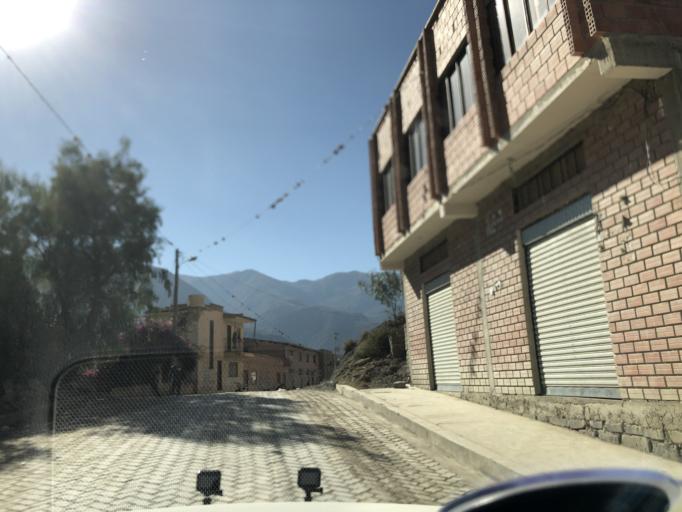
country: BO
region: La Paz
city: Patacamaya
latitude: -16.8884
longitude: -67.9507
